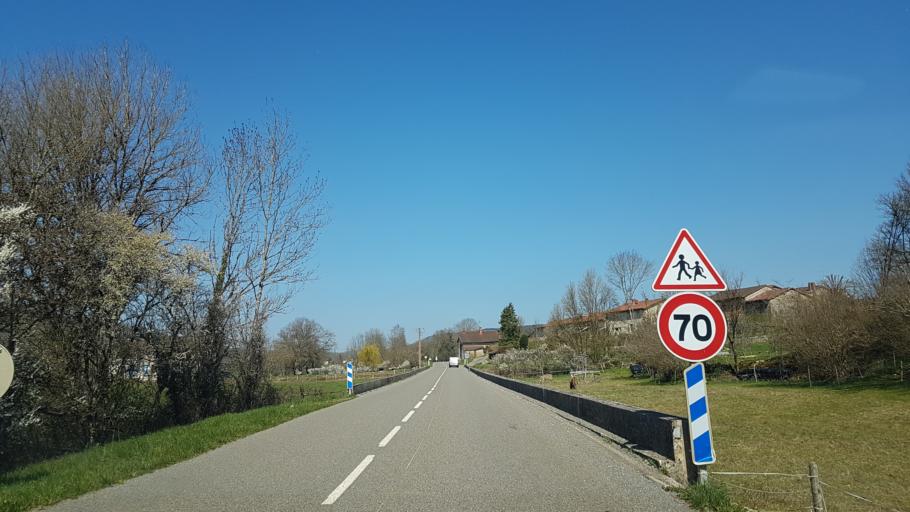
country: FR
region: Bourgogne
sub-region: Departement de Saone-et-Loire
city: Cuiseaux
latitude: 46.4685
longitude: 5.4493
